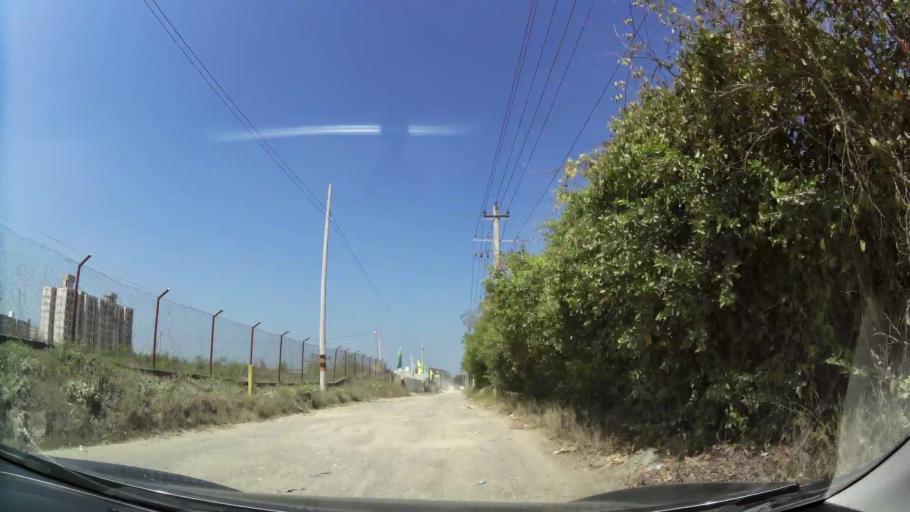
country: CO
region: Bolivar
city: Cartagena
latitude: 10.3985
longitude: -75.4546
